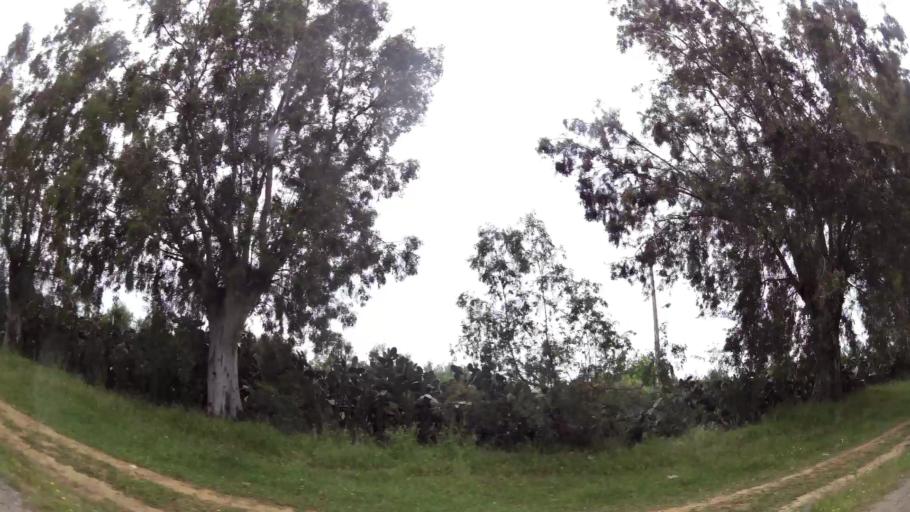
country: MA
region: Rabat-Sale-Zemmour-Zaer
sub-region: Khemisset
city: Tiflet
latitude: 33.8553
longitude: -6.2690
